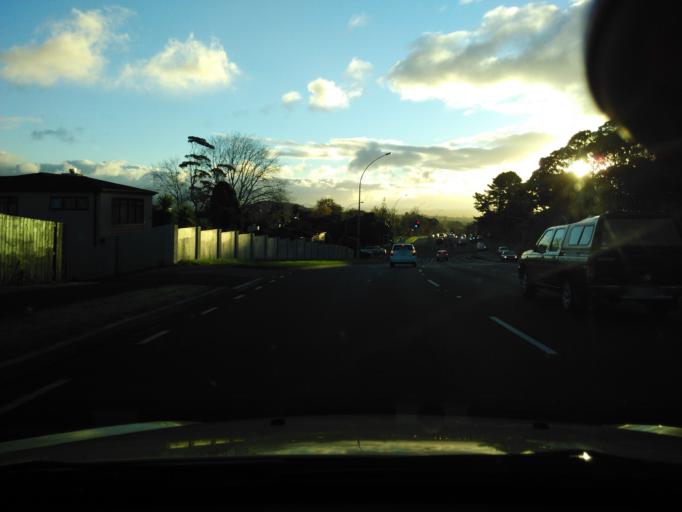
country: NZ
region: Auckland
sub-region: Auckland
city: Auckland
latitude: -36.8902
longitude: 174.7614
